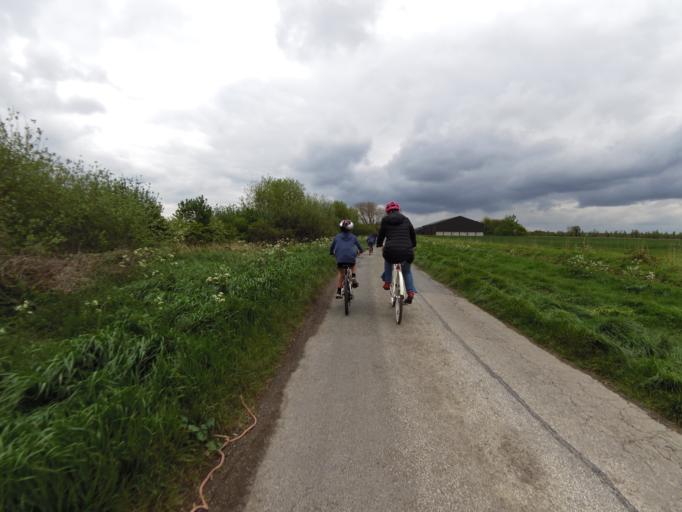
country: GB
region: England
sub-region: Cambridgeshire
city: Bottisham
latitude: 52.2703
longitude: 0.2812
